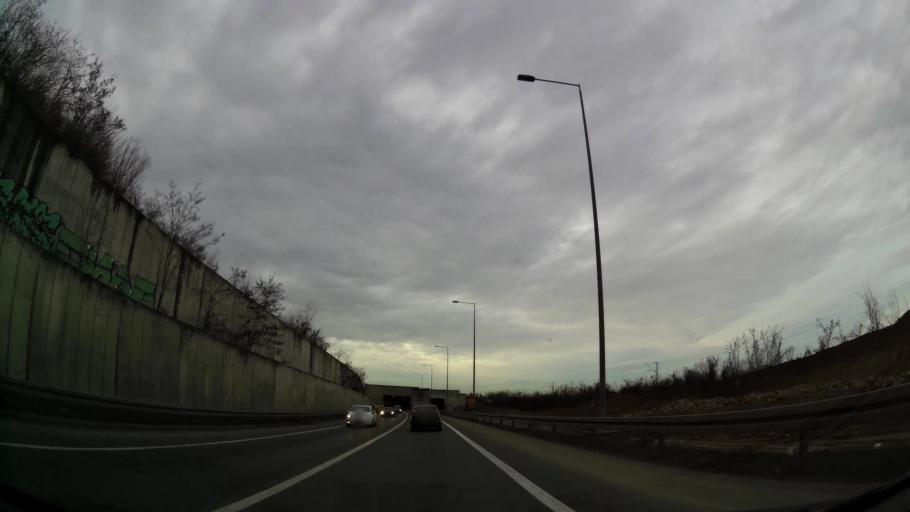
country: RS
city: Ostruznica
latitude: 44.7267
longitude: 20.3534
